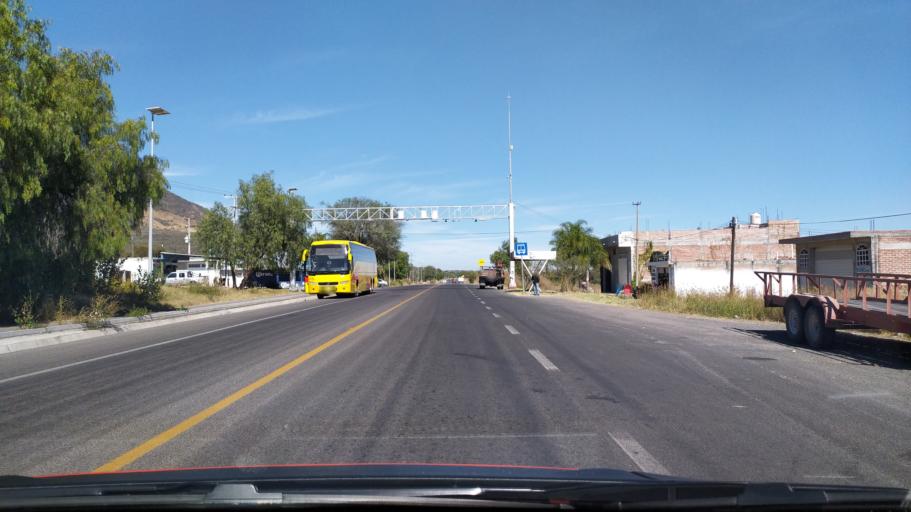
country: MX
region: Guanajuato
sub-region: Purisima del Rincon
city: Monte Grande
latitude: 20.9854
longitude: -101.8952
